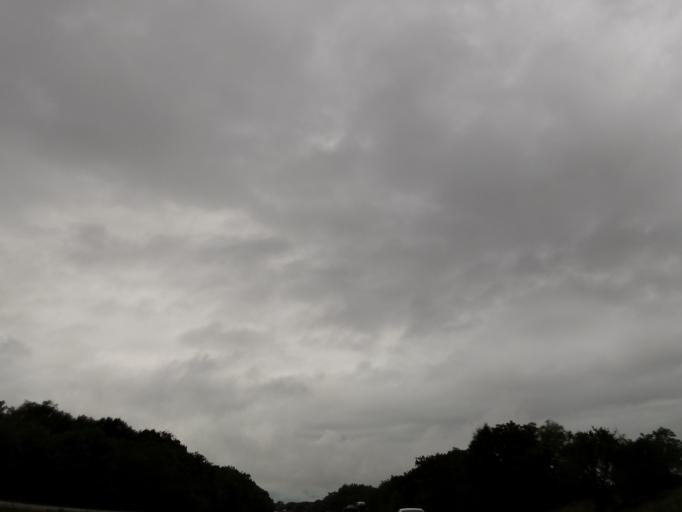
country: US
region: Illinois
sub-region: Jefferson County
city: Mount Vernon
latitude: 38.3554
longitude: -88.9956
